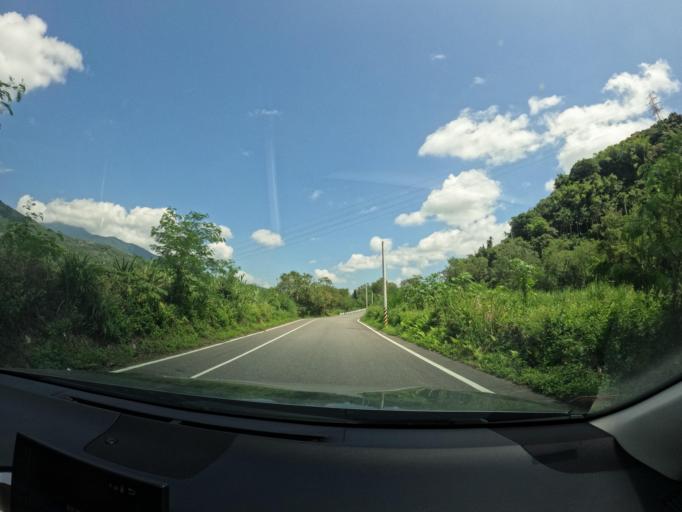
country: TW
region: Taiwan
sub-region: Hualien
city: Hualian
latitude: 23.6852
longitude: 121.4012
